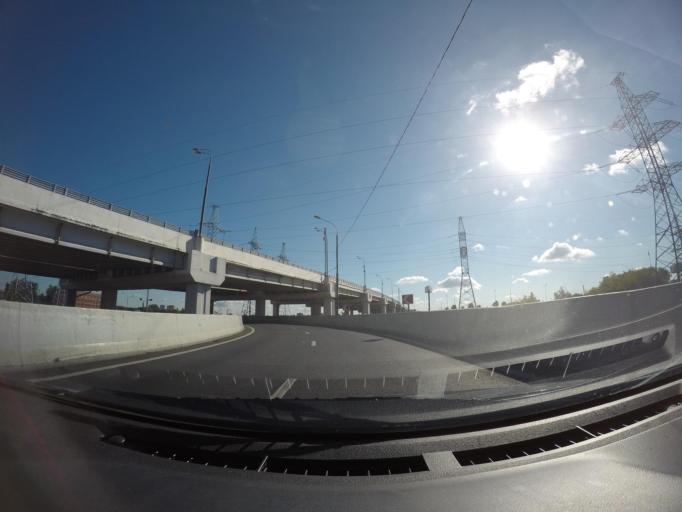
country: RU
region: Moscow
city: Veshnyaki
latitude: 55.7120
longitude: 37.8340
